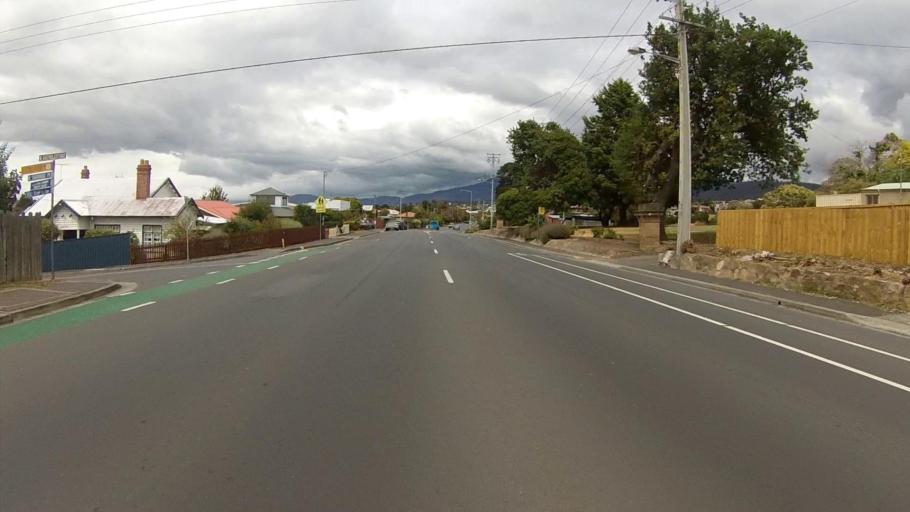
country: AU
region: Tasmania
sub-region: Glenorchy
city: Claremont
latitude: -42.7807
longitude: 147.2523
